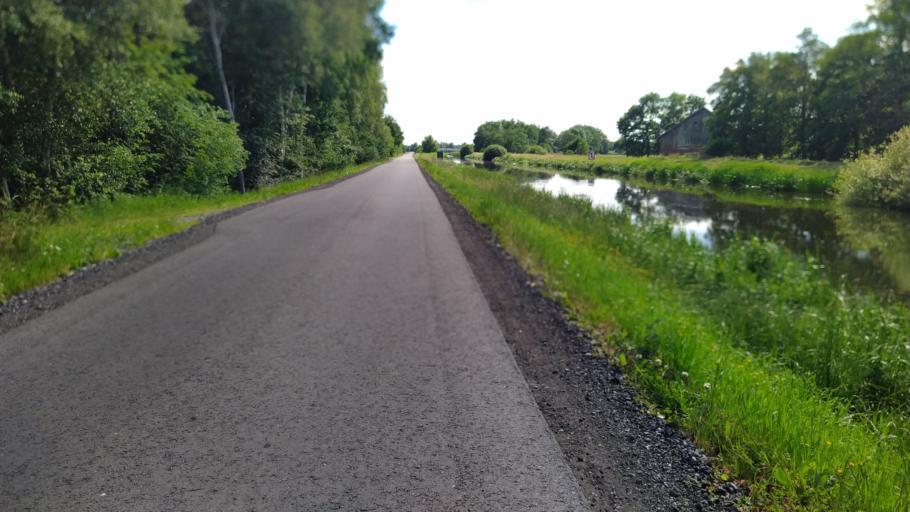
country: DE
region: Lower Saxony
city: Steinau
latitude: 53.6611
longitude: 8.9030
